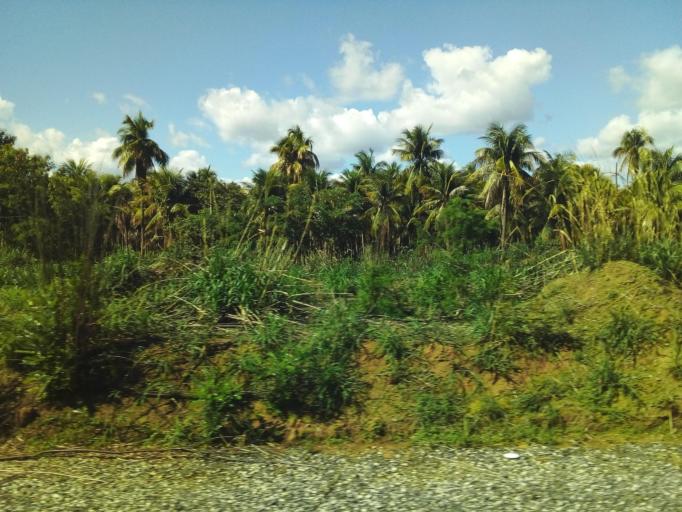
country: BR
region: Minas Gerais
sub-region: Governador Valadares
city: Governador Valadares
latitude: -18.8613
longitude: -41.8605
